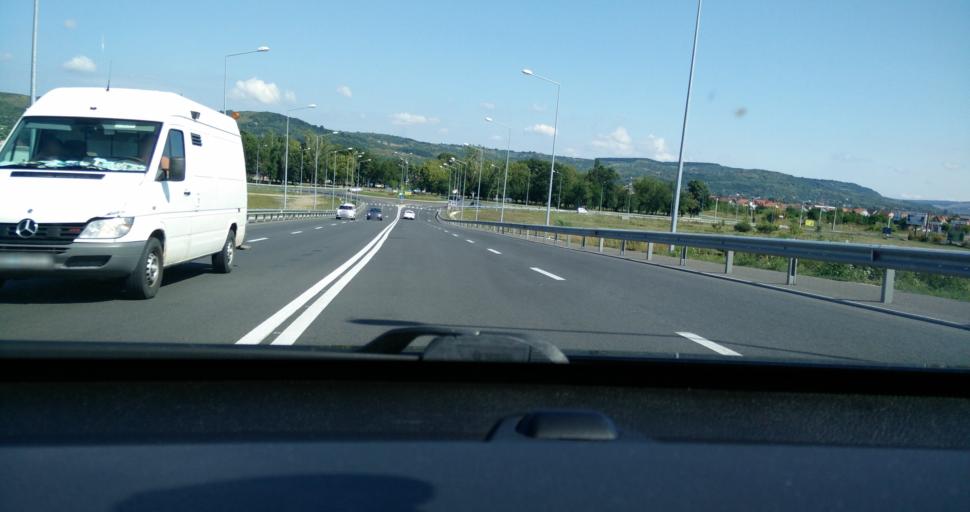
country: RO
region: Bihor
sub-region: Comuna Sanmartin
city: Sanmartin
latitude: 47.0344
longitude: 21.9961
